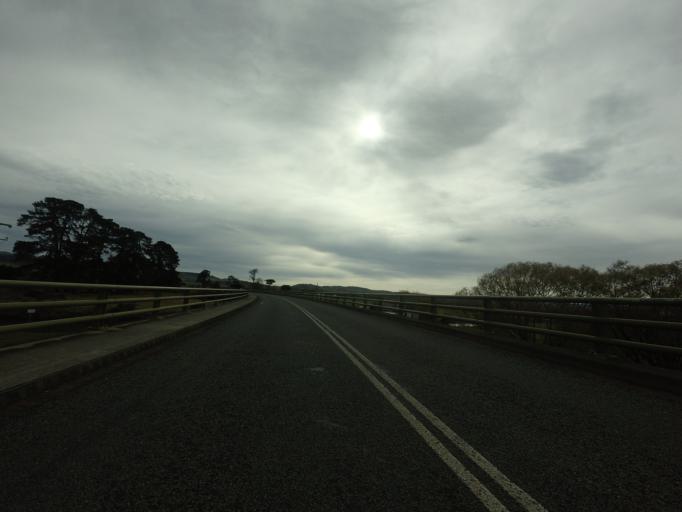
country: AU
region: Tasmania
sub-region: Derwent Valley
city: New Norfolk
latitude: -42.3793
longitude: 147.0029
